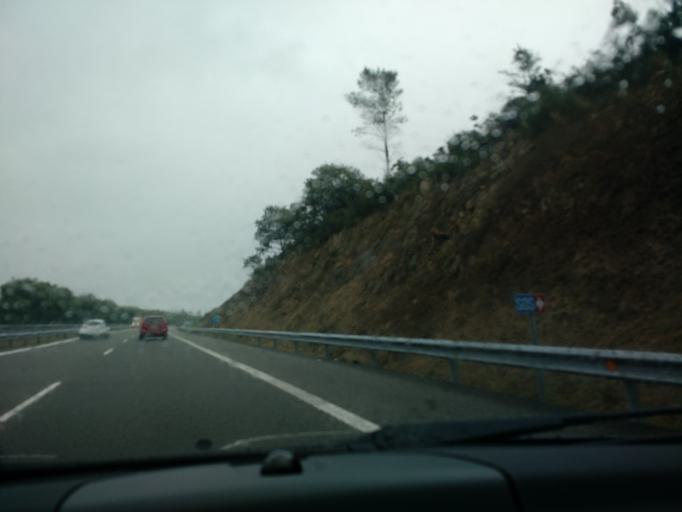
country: ES
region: Galicia
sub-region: Provincia da Coruna
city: Mesia
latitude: 43.1416
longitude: -8.3299
